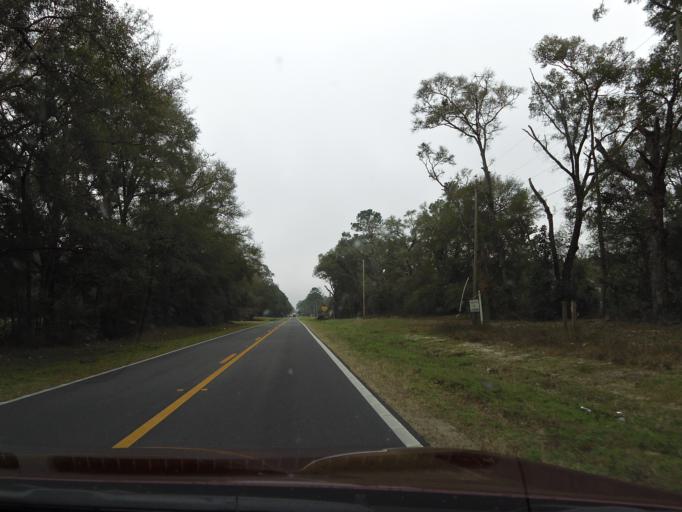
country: US
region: Florida
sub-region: Alachua County
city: High Springs
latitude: 29.8418
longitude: -82.5883
